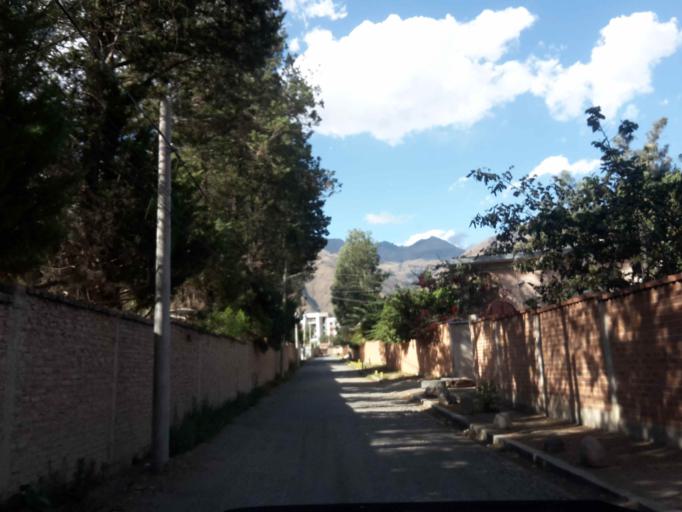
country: BO
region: Cochabamba
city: Cochabamba
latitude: -17.3555
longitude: -66.2000
